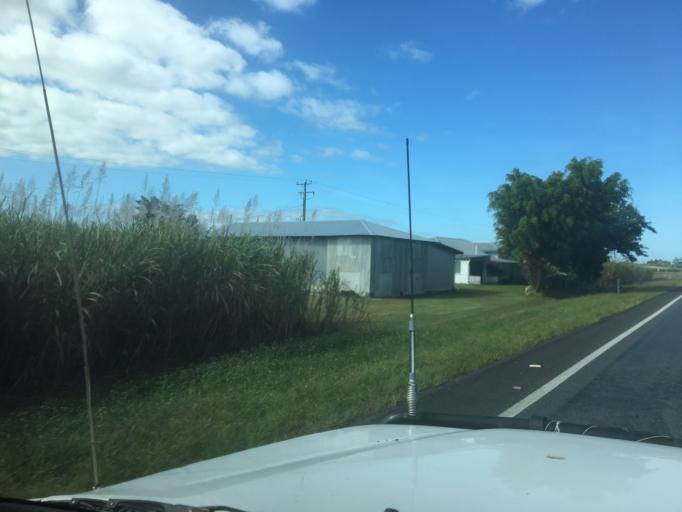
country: AU
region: Queensland
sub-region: Cassowary Coast
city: Innisfail
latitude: -17.3029
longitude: 145.9278
